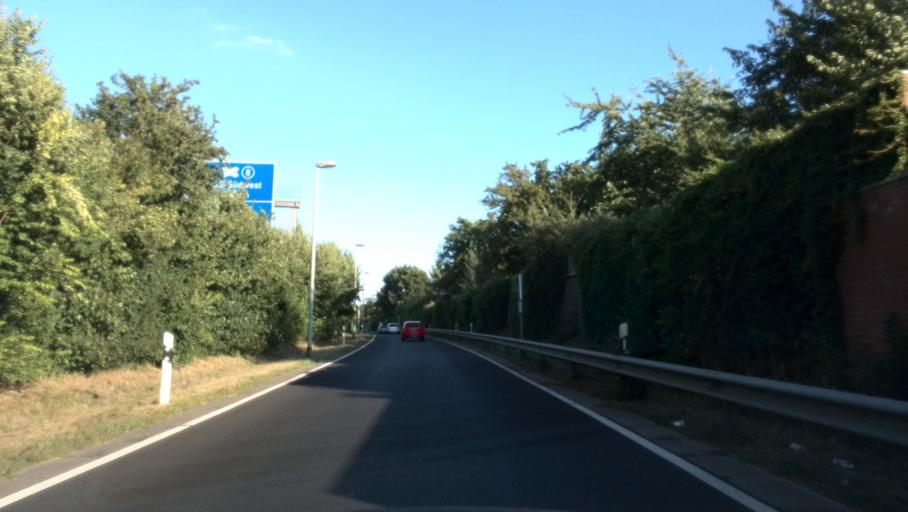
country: DE
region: Lower Saxony
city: Braunschweig
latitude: 52.2521
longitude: 10.4956
